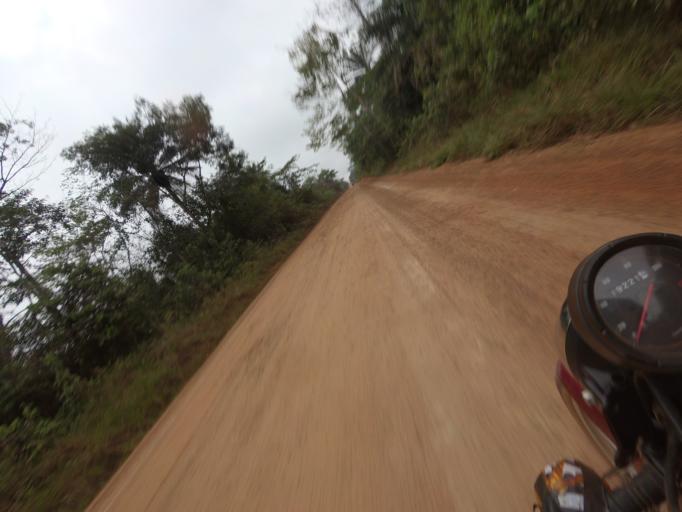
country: LR
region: Nimba
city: Sanniquellie
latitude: 7.3986
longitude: -8.6653
